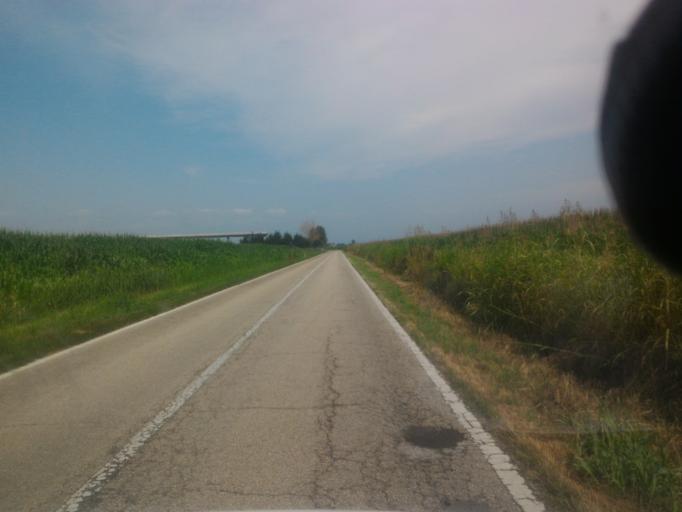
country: IT
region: Piedmont
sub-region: Provincia di Torino
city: Buriasco
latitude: 44.8613
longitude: 7.4203
